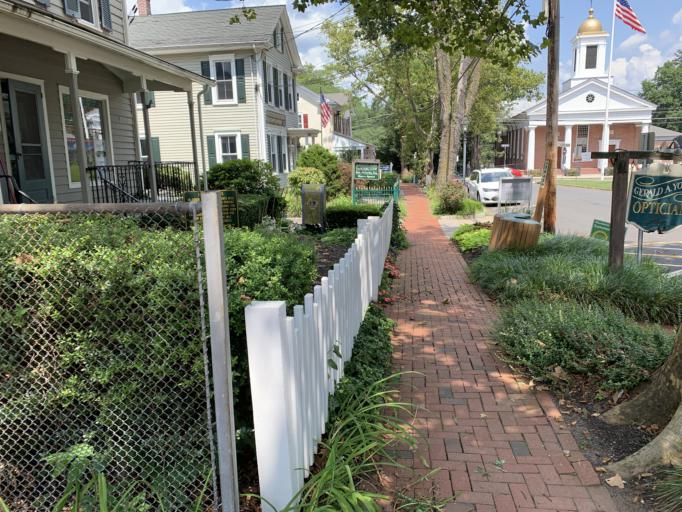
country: US
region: New Jersey
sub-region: Somerset County
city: Bernardsville
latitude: 40.7060
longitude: -74.5494
